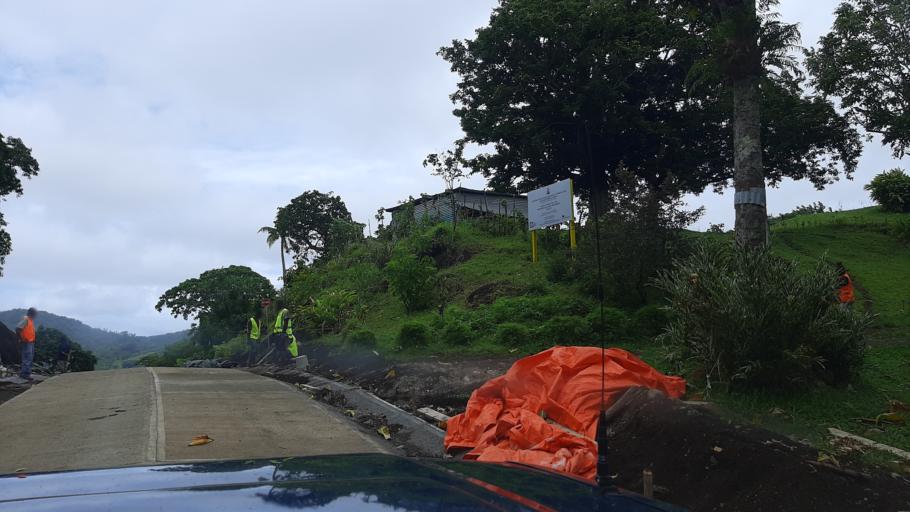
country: VU
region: Shefa
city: Port-Vila
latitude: -16.9001
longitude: 168.5738
